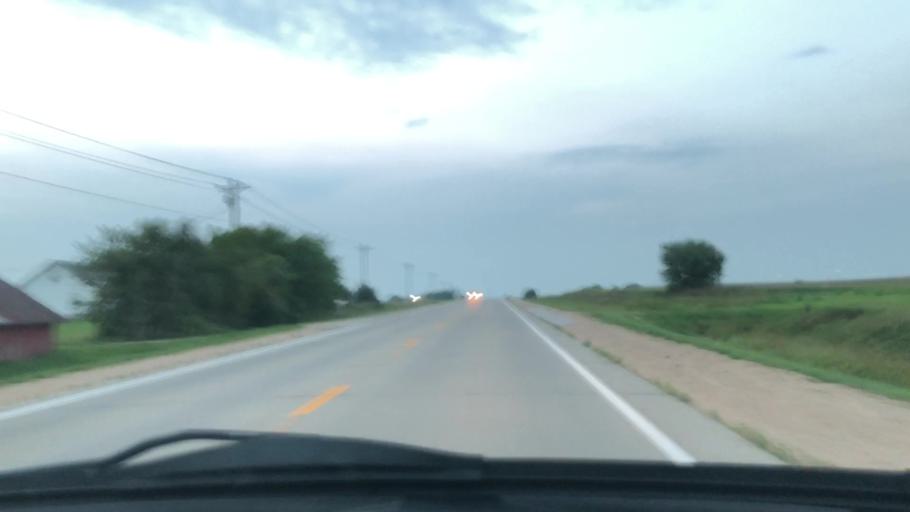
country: US
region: Iowa
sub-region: Linn County
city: Ely
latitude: 41.8569
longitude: -91.6754
